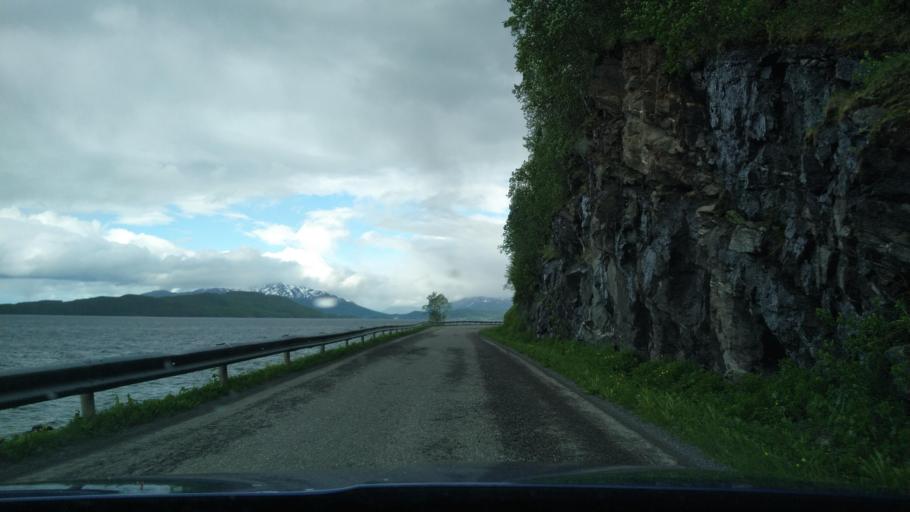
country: NO
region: Troms
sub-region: Lenvik
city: Finnsnes
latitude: 69.1414
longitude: 17.9138
